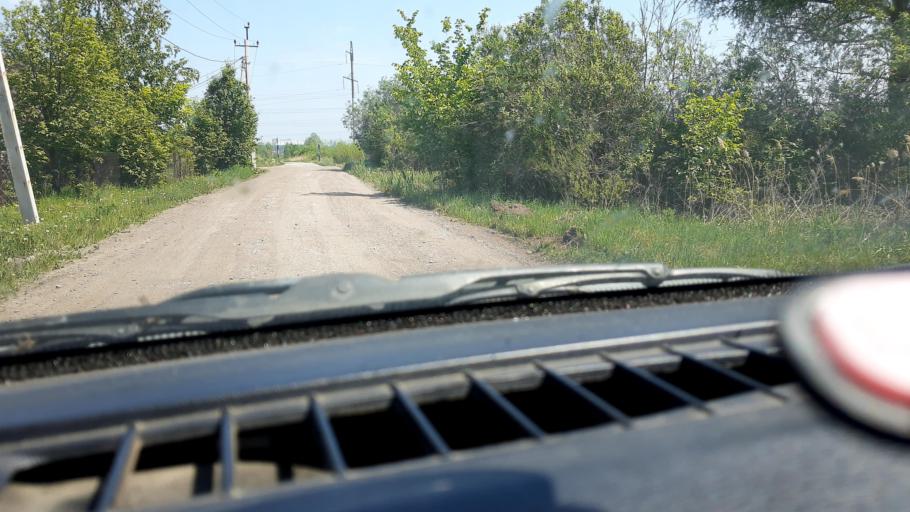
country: RU
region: Bashkortostan
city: Mikhaylovka
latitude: 54.7815
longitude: 55.8011
